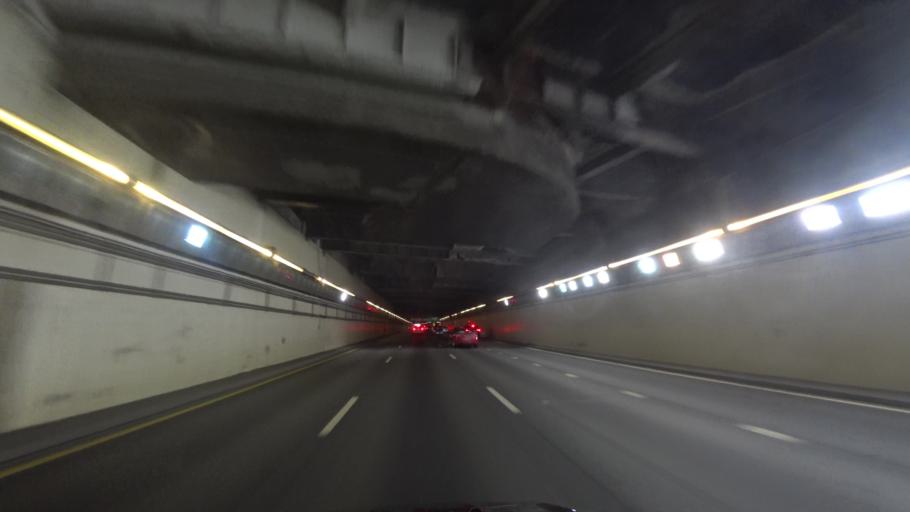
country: US
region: Massachusetts
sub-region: Suffolk County
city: Boston
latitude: 42.3476
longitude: -71.0837
